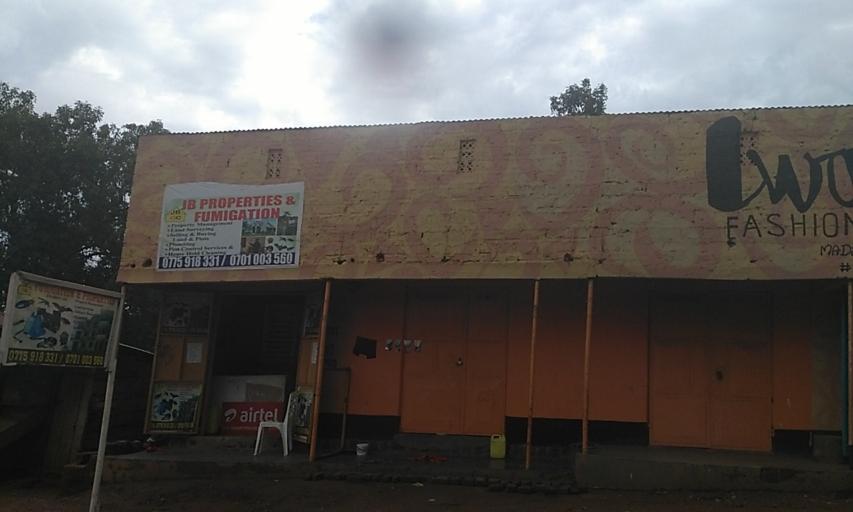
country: UG
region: Central Region
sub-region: Wakiso District
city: Kireka
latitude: 0.3698
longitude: 32.6412
